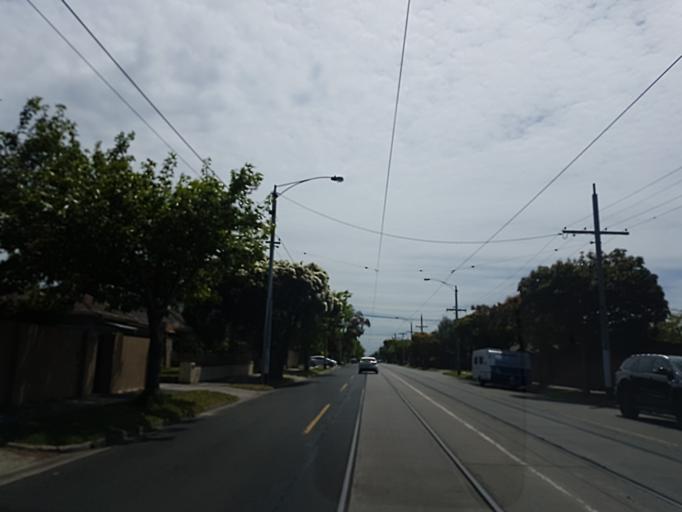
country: AU
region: Victoria
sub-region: Bayside
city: Brighton East
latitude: -37.8982
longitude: 145.0198
